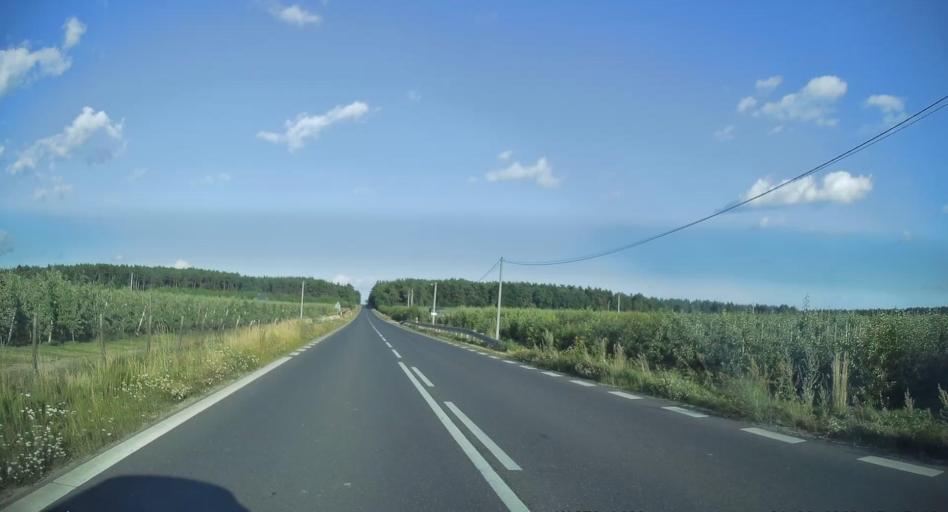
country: PL
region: Lodz Voivodeship
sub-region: Powiat rawski
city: Biala Rawska
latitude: 51.8026
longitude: 20.5067
